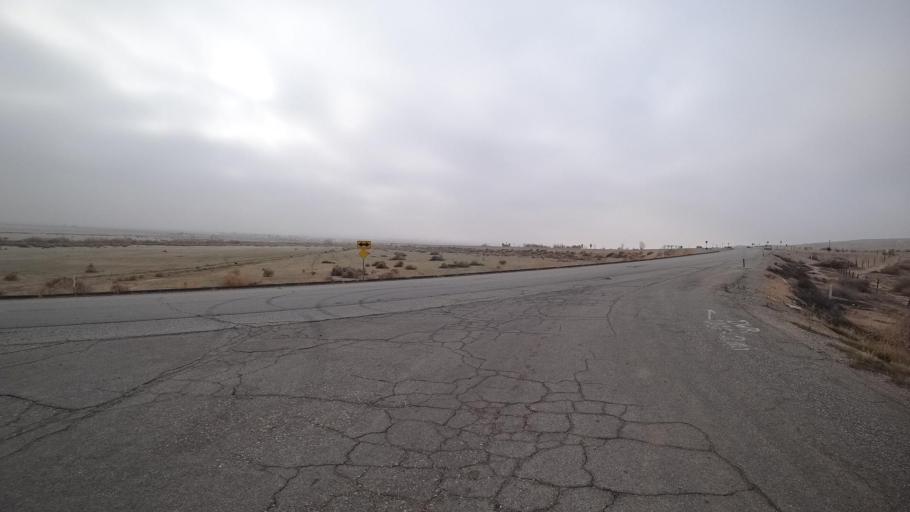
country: US
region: California
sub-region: Kern County
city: Maricopa
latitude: 35.1292
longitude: -119.3670
